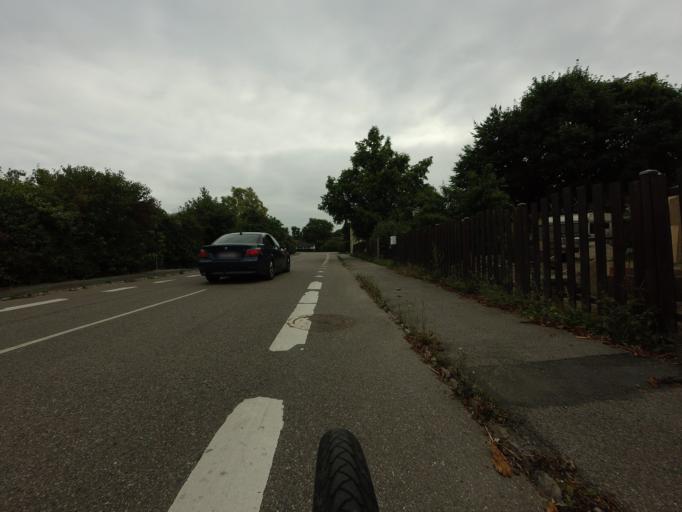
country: DK
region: Zealand
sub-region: Stevns Kommune
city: Store Heddinge
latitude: 55.2816
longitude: 12.4339
